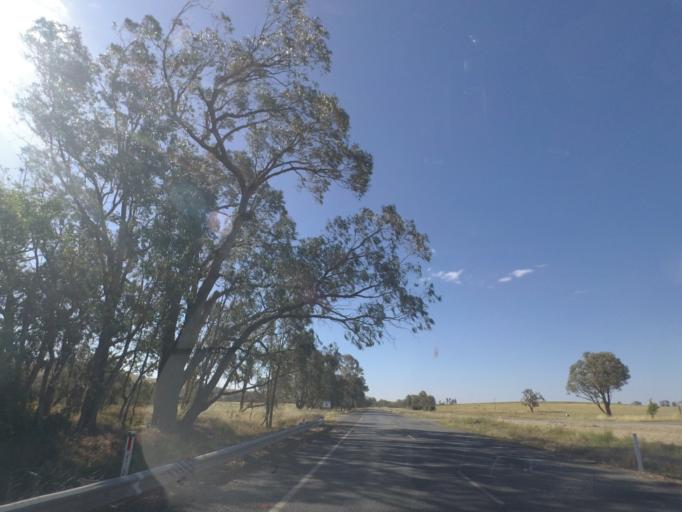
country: AU
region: New South Wales
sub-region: Greater Hume Shire
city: Holbrook
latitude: -35.7907
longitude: 147.2764
